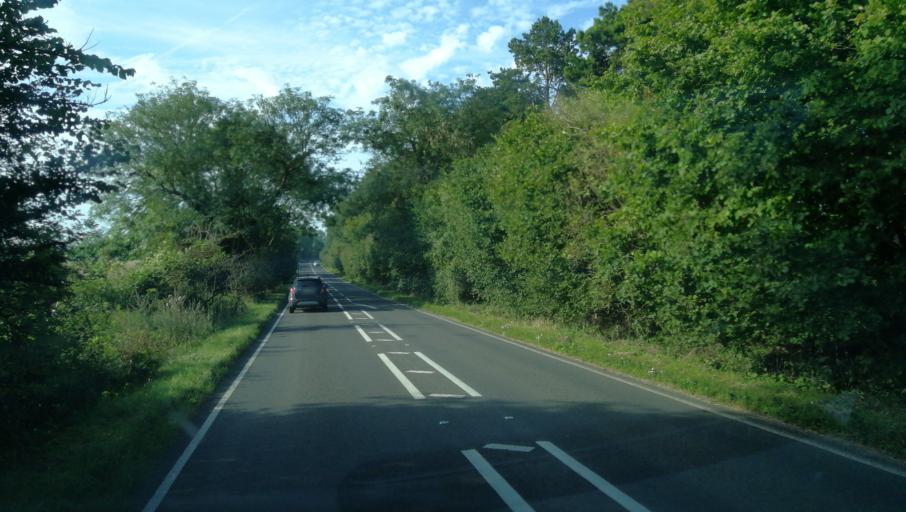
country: GB
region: England
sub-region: Oxfordshire
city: Somerton
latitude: 51.9199
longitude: -1.3250
